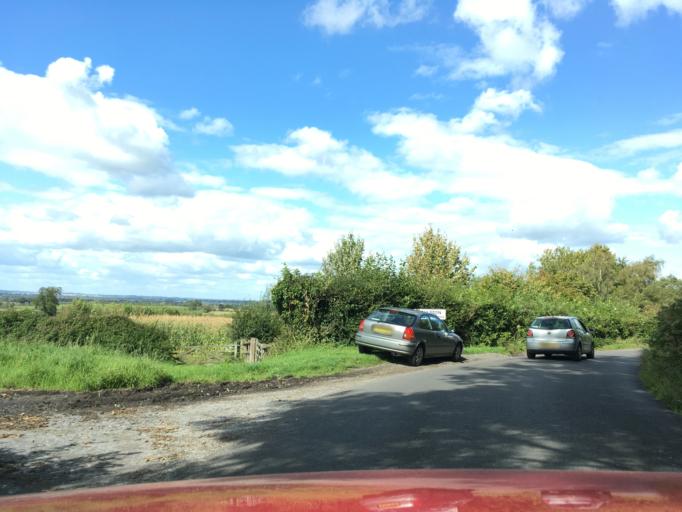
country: GB
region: England
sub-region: Wiltshire
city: Erlestoke
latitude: 51.2831
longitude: -2.0771
